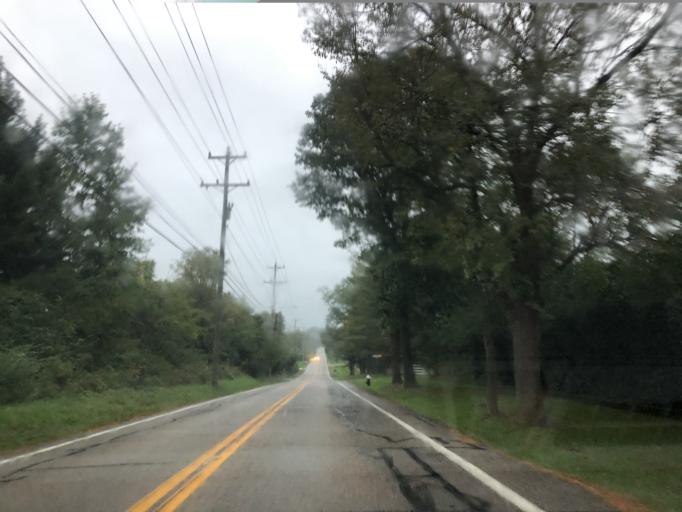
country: US
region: Ohio
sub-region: Hamilton County
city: The Village of Indian Hill
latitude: 39.2401
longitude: -84.3111
